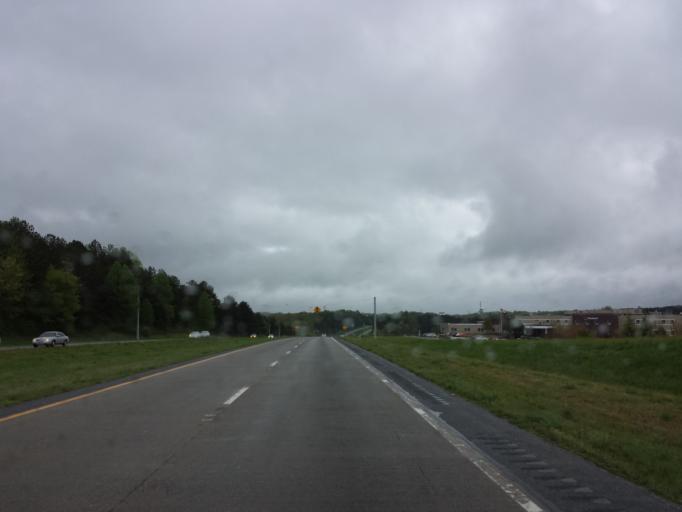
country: US
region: Georgia
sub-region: Pickens County
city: Jasper
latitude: 34.4490
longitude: -84.4483
